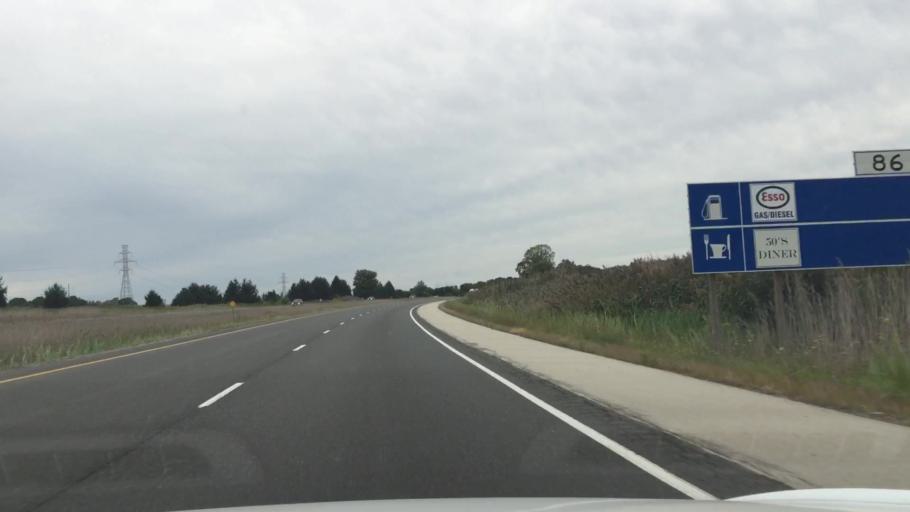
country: CA
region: Ontario
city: Delaware
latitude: 42.8942
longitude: -81.4108
